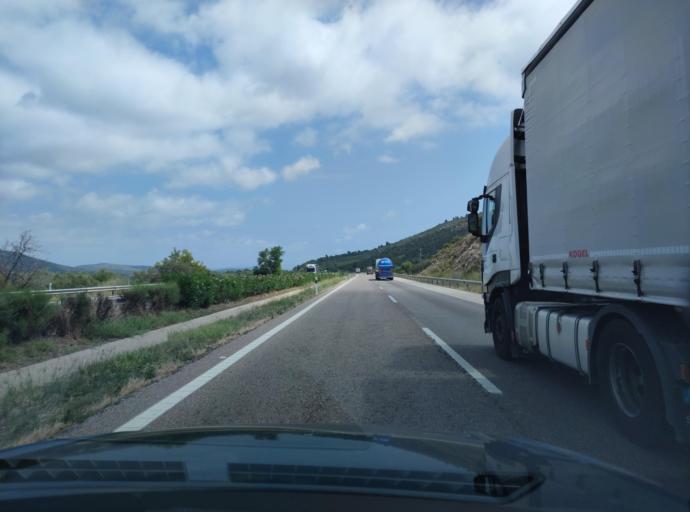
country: ES
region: Valencia
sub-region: Provincia de Castello
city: Santa Magdalena de Pulpis
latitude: 40.3756
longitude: 0.3366
